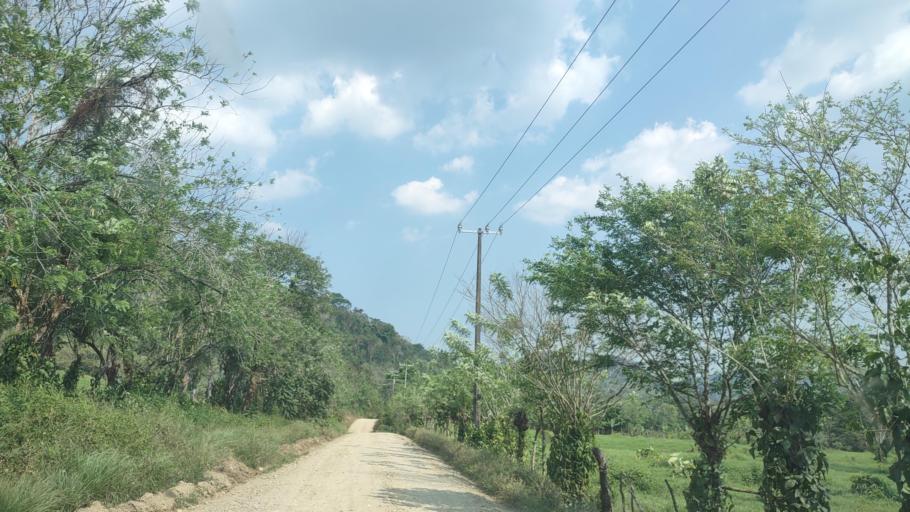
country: MX
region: Chiapas
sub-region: Tecpatan
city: Raudales Malpaso
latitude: 17.3320
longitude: -93.7500
